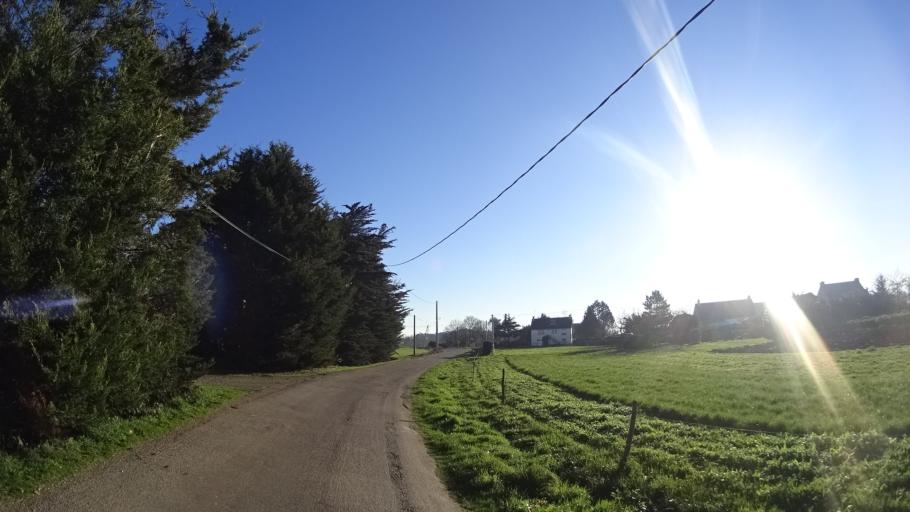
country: FR
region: Brittany
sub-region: Departement du Morbihan
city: Allaire
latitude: 47.6571
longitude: -2.1734
